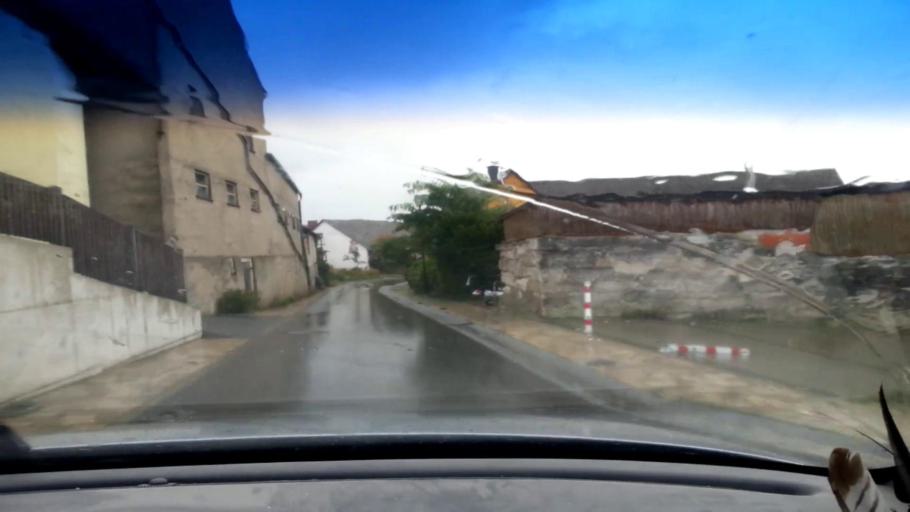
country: DE
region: Bavaria
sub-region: Upper Franconia
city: Priesendorf
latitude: 49.8625
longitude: 10.7228
